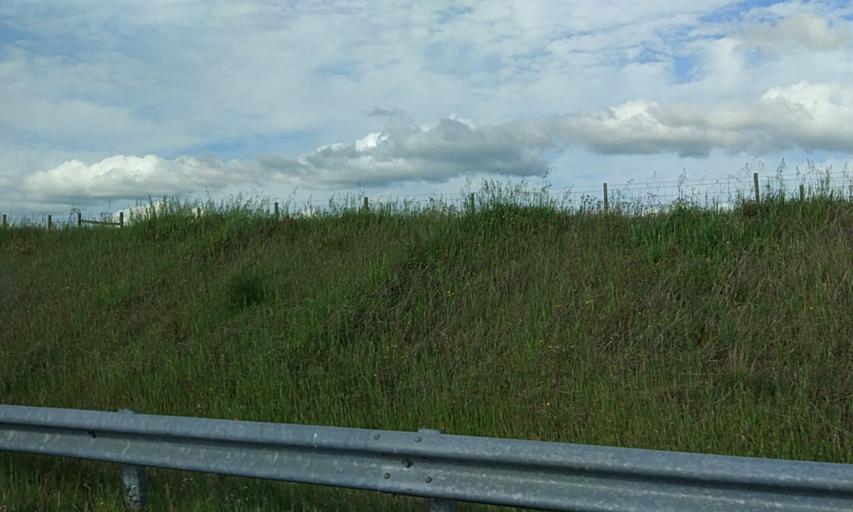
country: PT
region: Evora
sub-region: Evora
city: Evora
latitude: 38.6447
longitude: -7.8558
